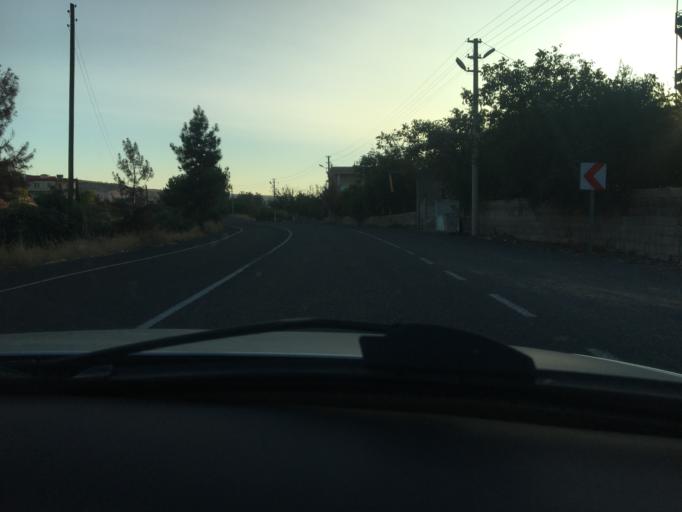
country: TR
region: Sanliurfa
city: Halfeti
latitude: 37.2206
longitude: 37.9548
